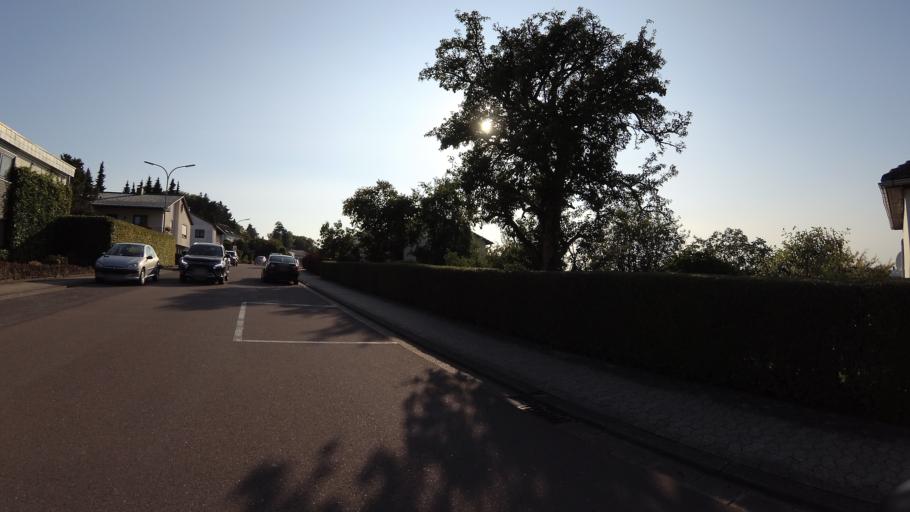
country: DE
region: Saarland
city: Gersheim
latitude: 49.1932
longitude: 7.1455
